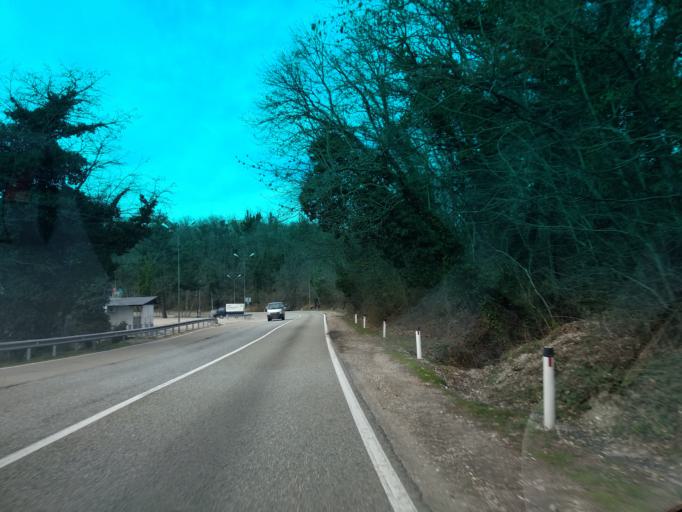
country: RU
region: Krasnodarskiy
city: Shepsi
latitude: 44.0759
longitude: 39.1345
